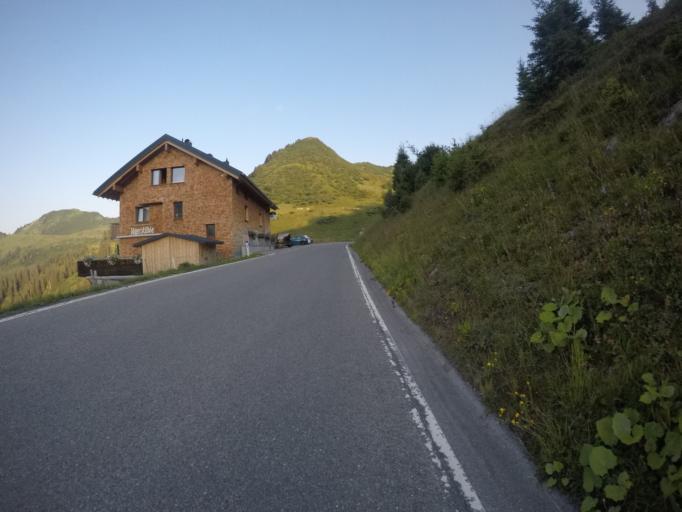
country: AT
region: Vorarlberg
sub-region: Politischer Bezirk Bregenz
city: Damuels
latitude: 47.2790
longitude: 9.8542
